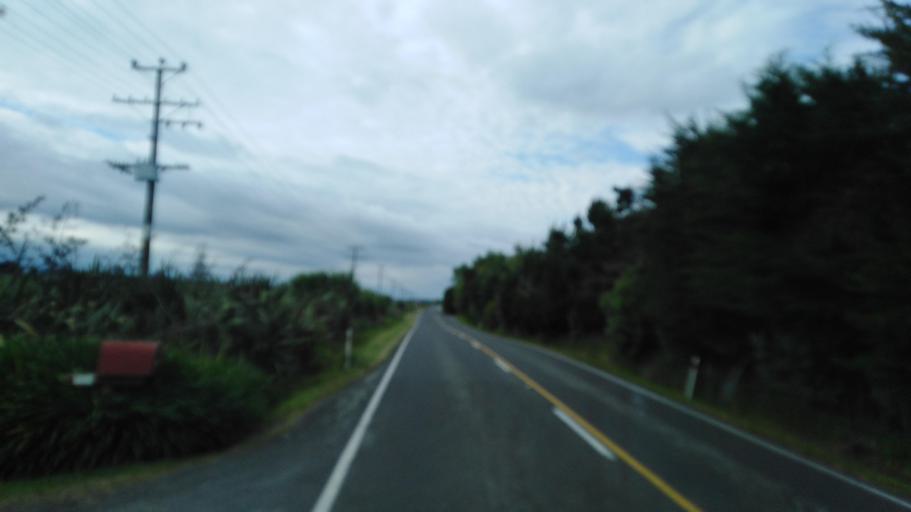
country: NZ
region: Manawatu-Wanganui
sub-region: Rangitikei District
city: Bulls
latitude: -40.1214
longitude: 175.3555
